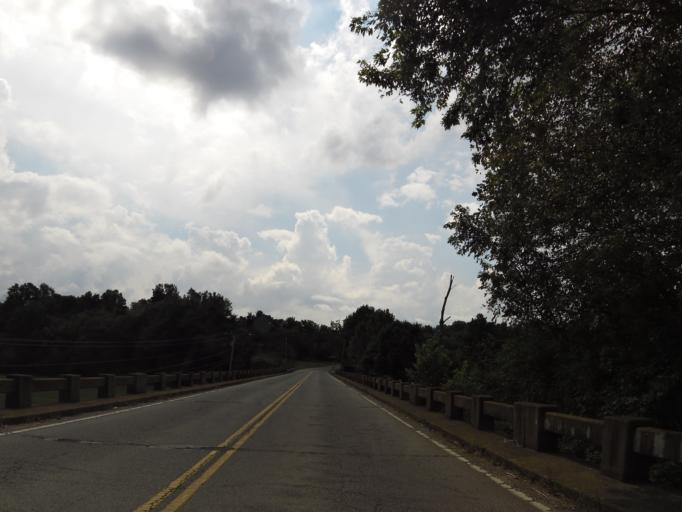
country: US
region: Tennessee
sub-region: Perry County
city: Linden
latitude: 35.8118
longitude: -87.7785
